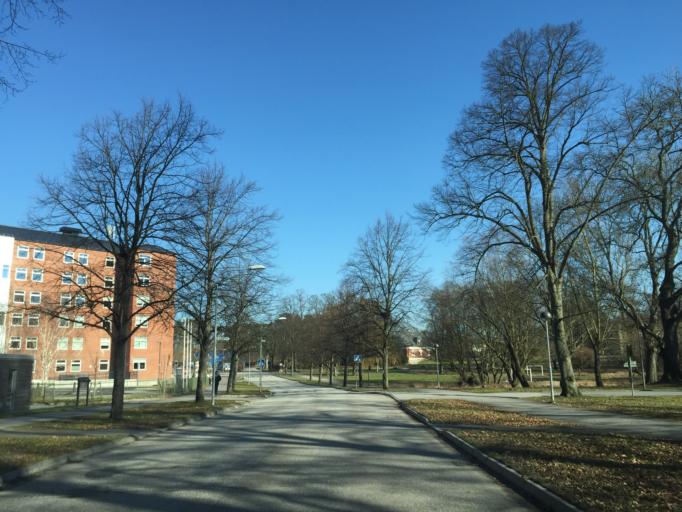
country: SE
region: Skane
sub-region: Lunds Kommun
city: Lund
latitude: 55.6867
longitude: 13.1813
